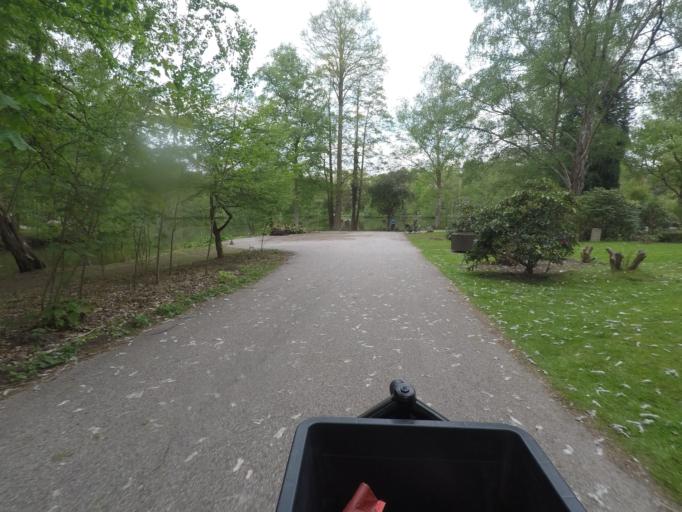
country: DE
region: Hamburg
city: Wellingsbuettel
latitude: 53.6274
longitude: 10.0675
